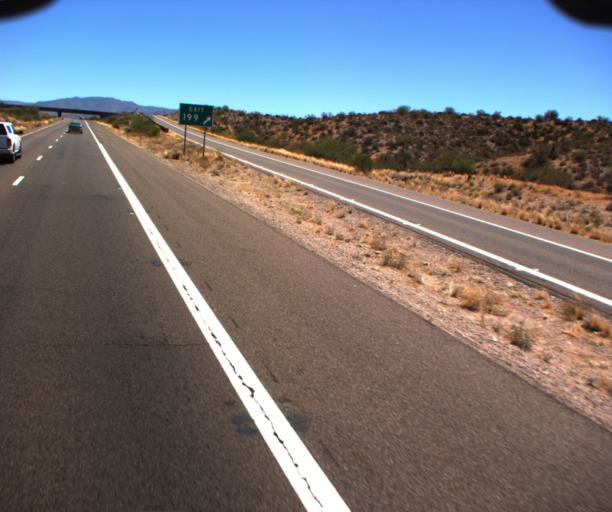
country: US
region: Arizona
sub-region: Maricopa County
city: Rio Verde
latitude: 33.6243
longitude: -111.5629
